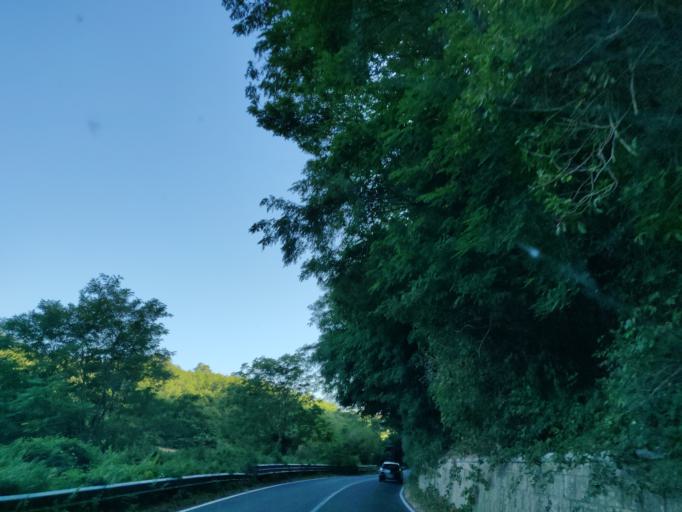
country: IT
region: Latium
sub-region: Provincia di Viterbo
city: Gradoli
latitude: 42.6562
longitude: 11.8474
